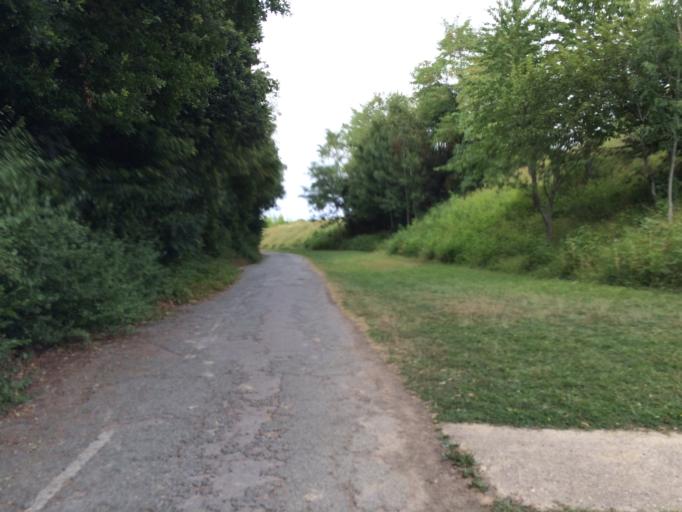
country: FR
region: Ile-de-France
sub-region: Departement de l'Essonne
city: Quincy-sous-Senart
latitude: 48.6576
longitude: 2.5482
